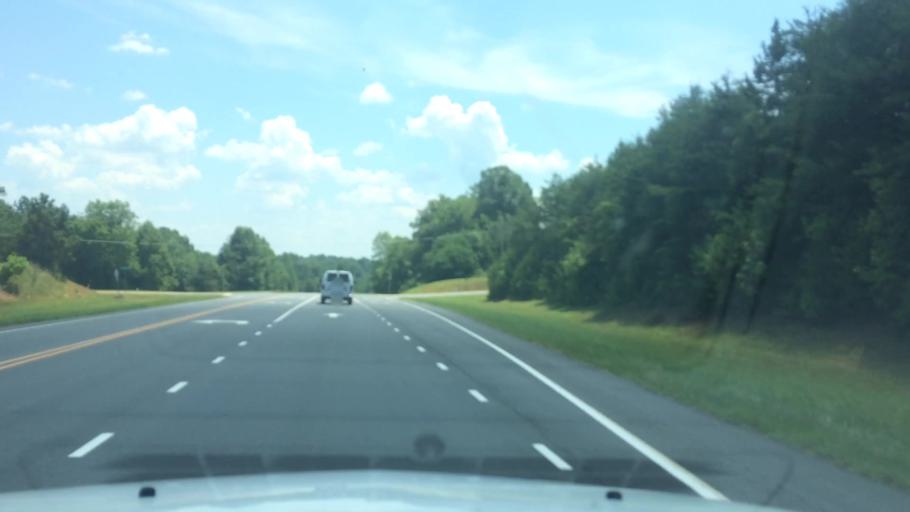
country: US
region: North Carolina
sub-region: Alexander County
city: Stony Point
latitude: 35.8368
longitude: -81.0208
